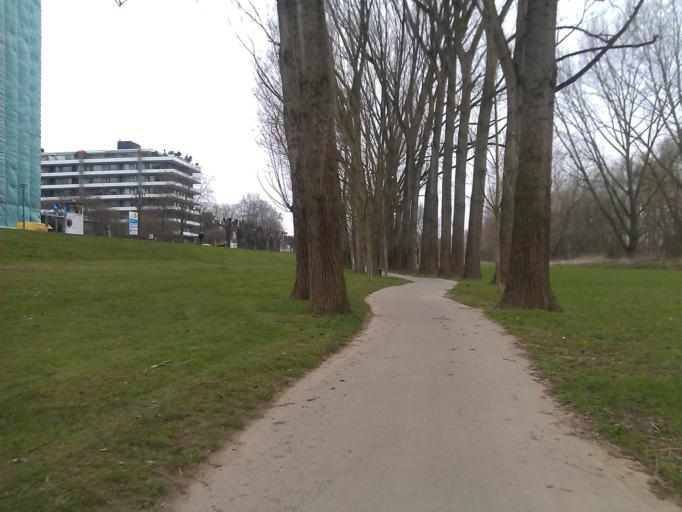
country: DE
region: North Rhine-Westphalia
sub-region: Regierungsbezirk Koln
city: Poll
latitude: 50.8919
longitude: 7.0115
